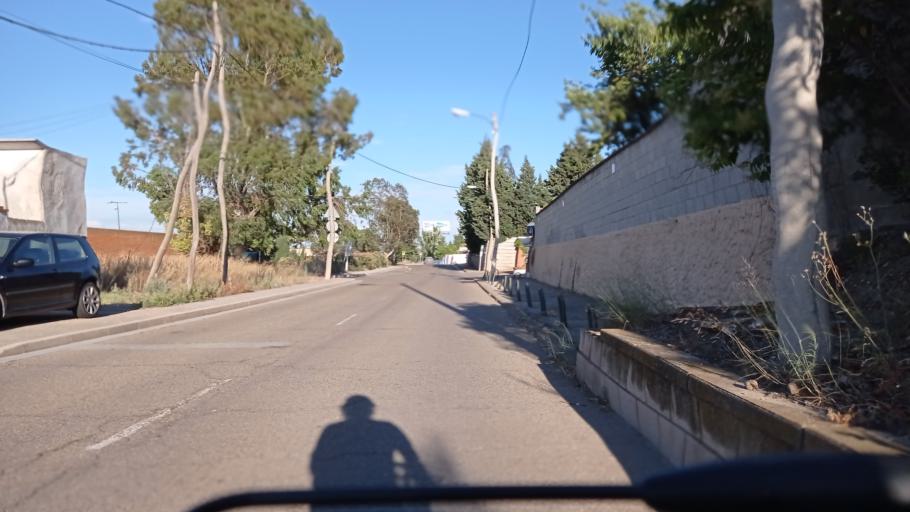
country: ES
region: Aragon
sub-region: Provincia de Zaragoza
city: Oliver-Valdefierro, Oliver, Valdefierro
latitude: 41.6731
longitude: -0.9532
